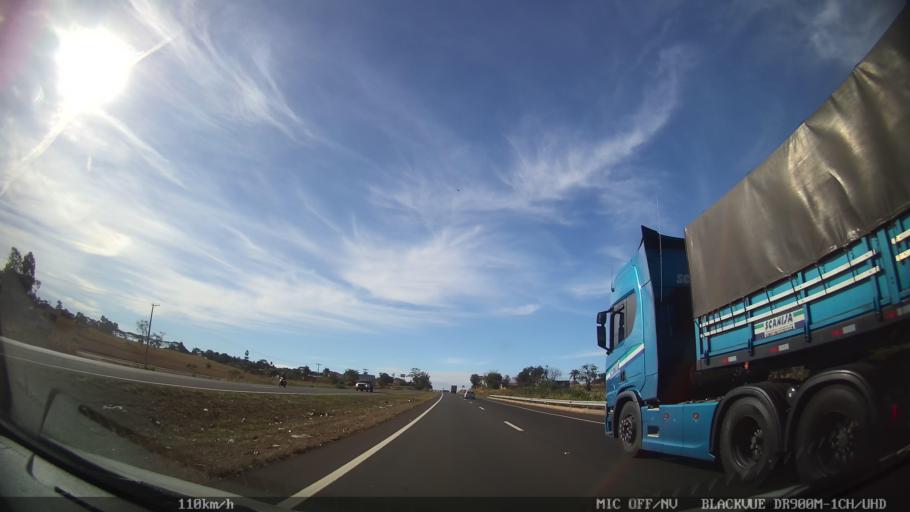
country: BR
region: Sao Paulo
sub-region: Sao Jose Do Rio Preto
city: Sao Jose do Rio Preto
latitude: -20.7504
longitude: -49.3412
